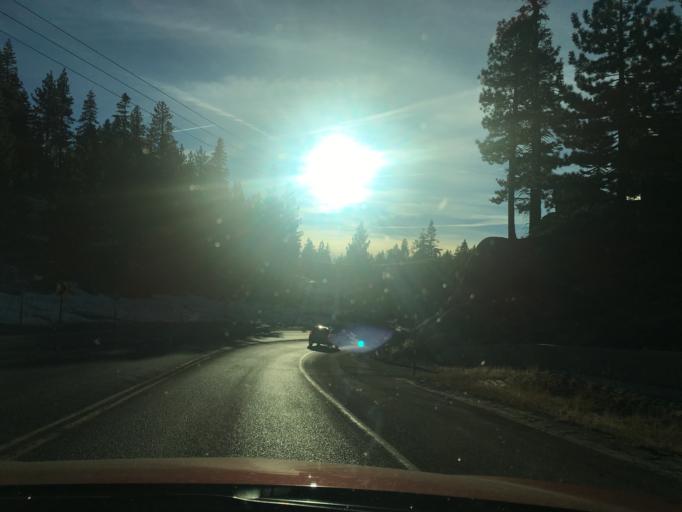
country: US
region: Nevada
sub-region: Douglas County
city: Kingsbury
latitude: 38.9736
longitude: -119.8988
